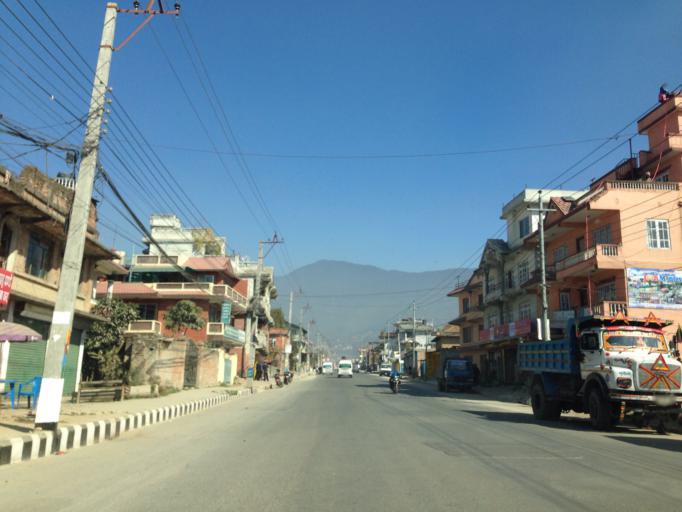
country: NP
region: Central Region
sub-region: Bagmati Zone
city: Kathmandu
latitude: 27.7579
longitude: 85.3501
